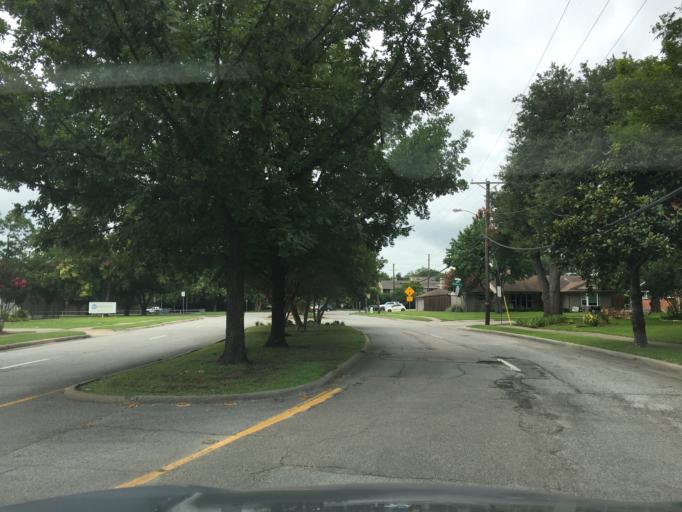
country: US
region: Texas
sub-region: Dallas County
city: Highland Park
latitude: 32.8564
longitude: -96.7417
